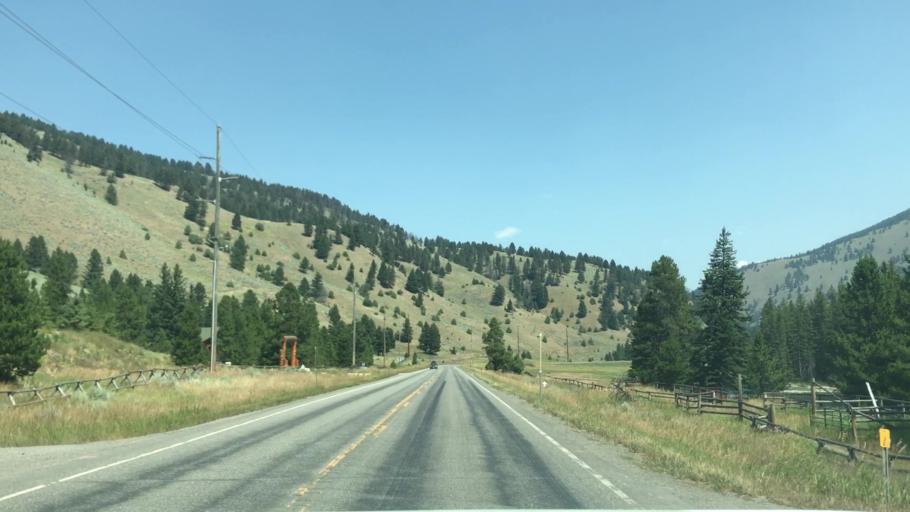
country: US
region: Montana
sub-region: Gallatin County
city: Big Sky
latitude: 45.2728
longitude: -111.2413
